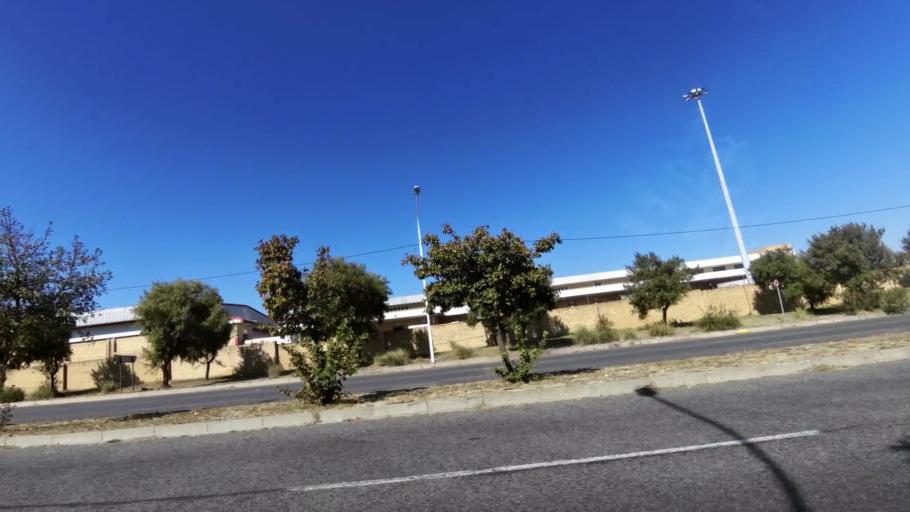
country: ZA
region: Gauteng
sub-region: City of Johannesburg Metropolitan Municipality
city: Johannesburg
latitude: -26.2492
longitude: 27.9728
